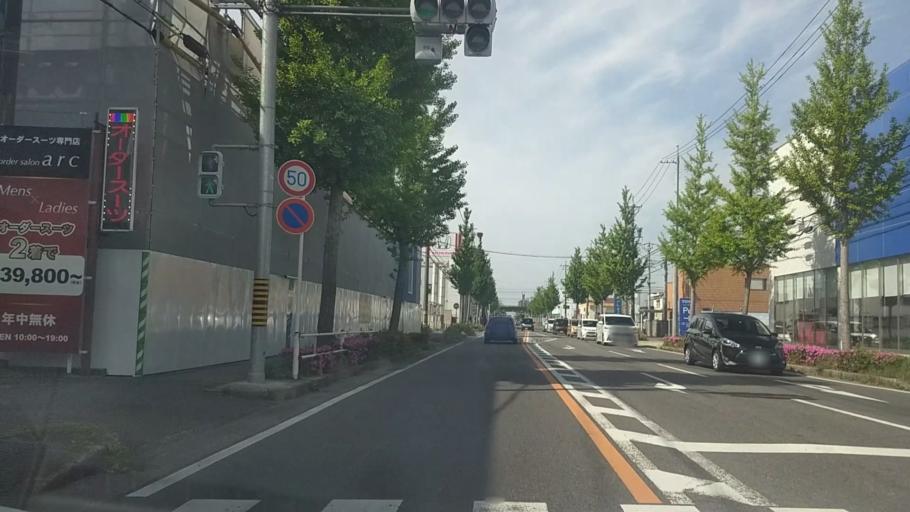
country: JP
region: Aichi
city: Okazaki
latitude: 34.9408
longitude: 137.1510
